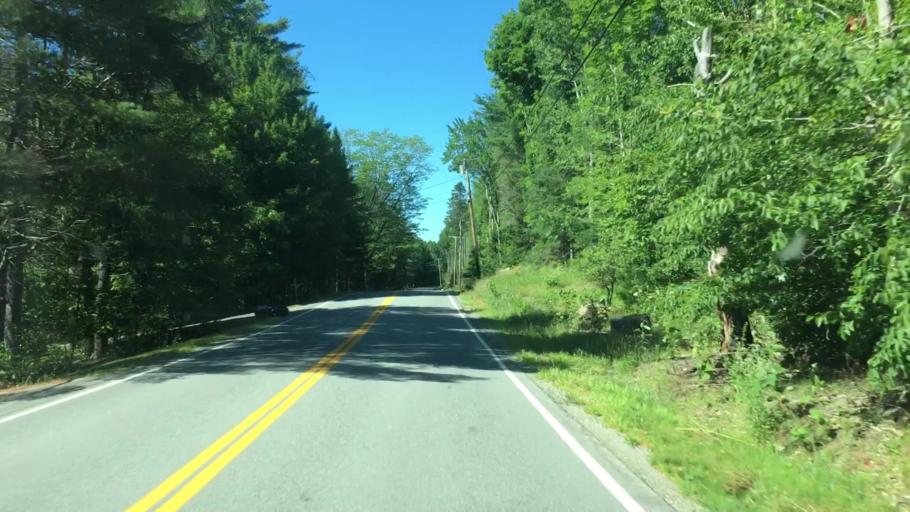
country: US
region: Maine
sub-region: Hancock County
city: Dedham
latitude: 44.7194
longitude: -68.6413
